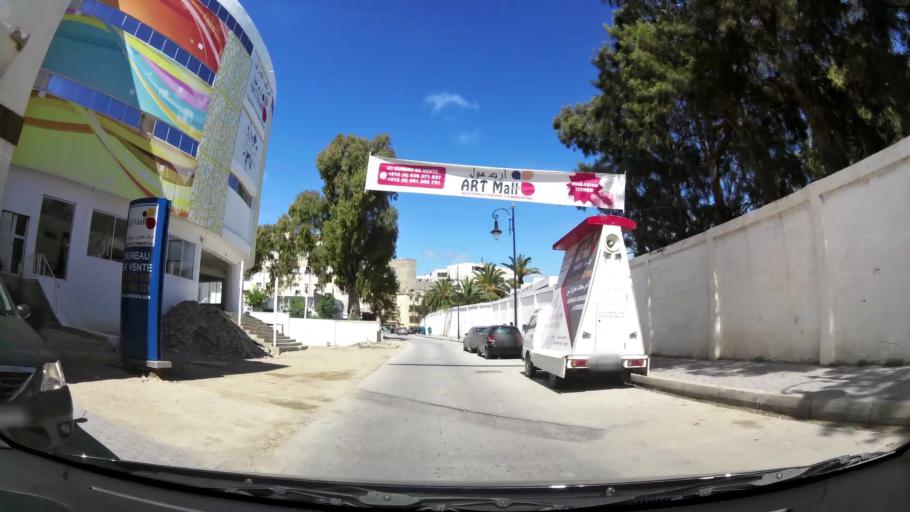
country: MA
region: Tanger-Tetouan
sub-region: Tanger-Assilah
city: Tangier
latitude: 35.7854
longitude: -5.8229
